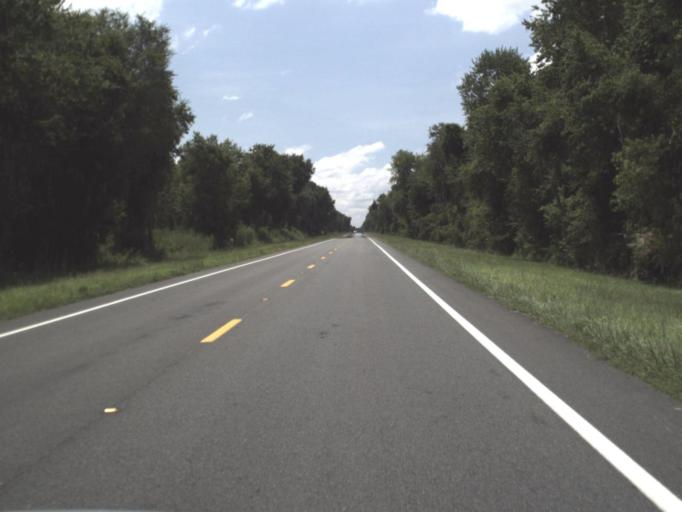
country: US
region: Florida
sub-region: Hamilton County
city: Jasper
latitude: 30.4118
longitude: -82.8471
